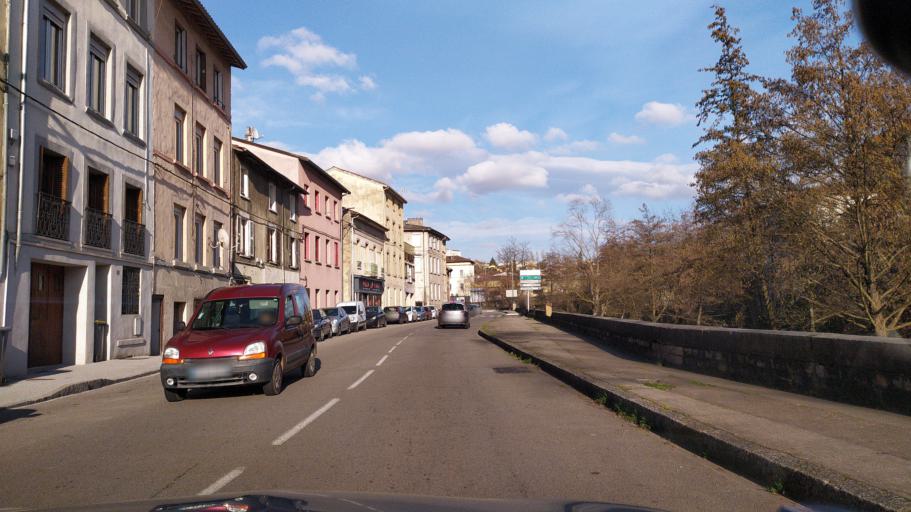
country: FR
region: Rhone-Alpes
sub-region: Departement de l'Isere
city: Pont-Eveque
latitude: 45.5287
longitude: 4.9002
